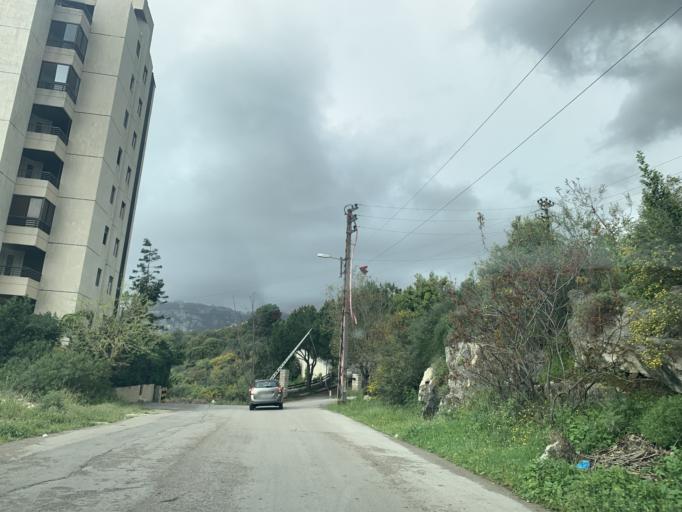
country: LB
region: Mont-Liban
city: Djounie
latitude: 34.0024
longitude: 35.6525
